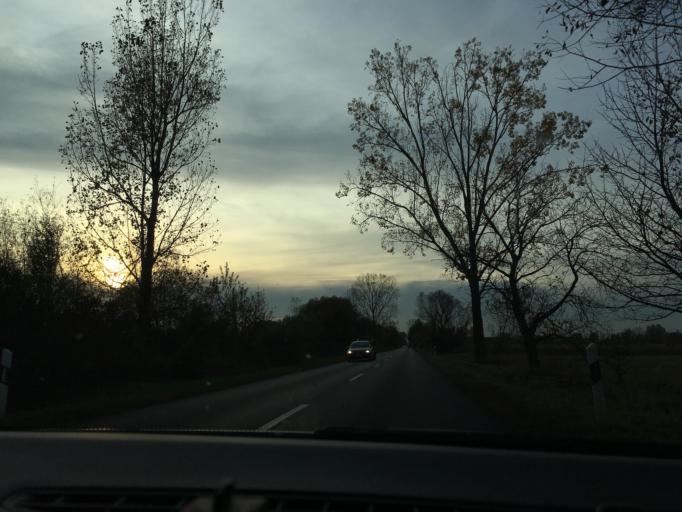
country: HU
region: Szabolcs-Szatmar-Bereg
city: Kisleta
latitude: 47.8545
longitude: 21.9973
